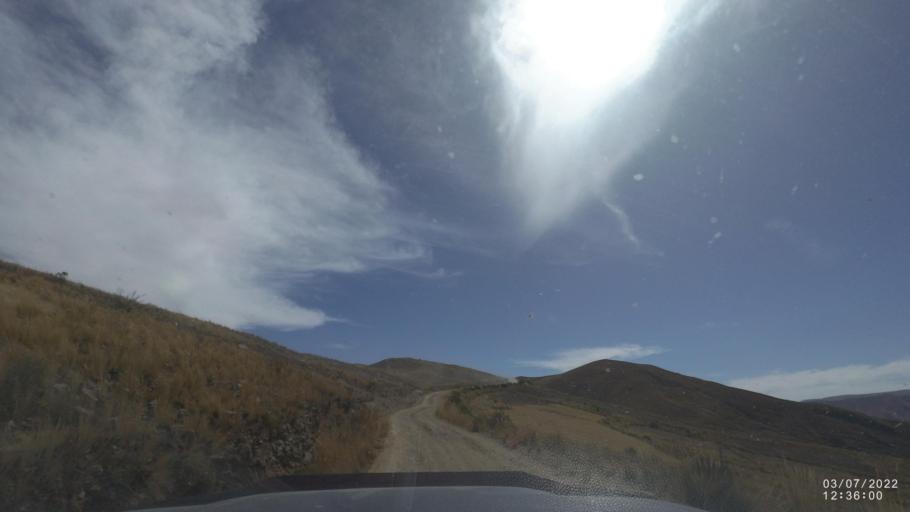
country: BO
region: Cochabamba
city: Irpa Irpa
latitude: -17.8039
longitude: -66.6114
